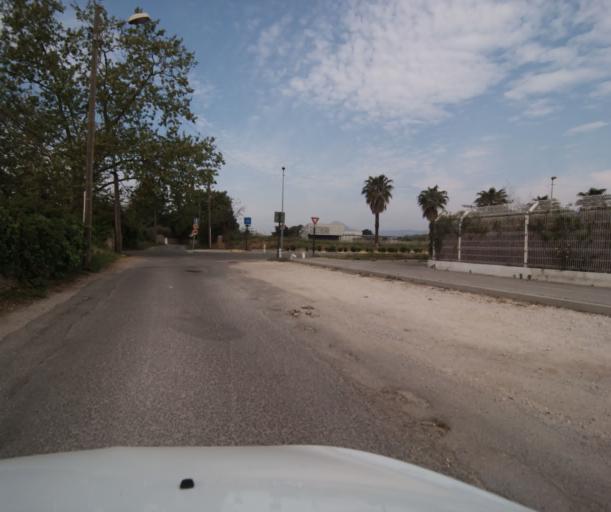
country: FR
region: Provence-Alpes-Cote d'Azur
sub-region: Departement du Var
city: Hyeres
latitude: 43.1166
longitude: 6.1160
